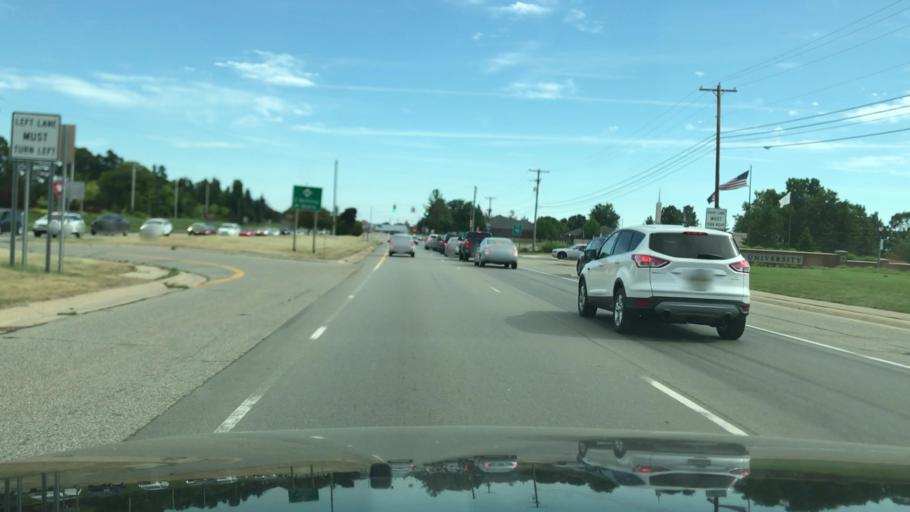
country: US
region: Michigan
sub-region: Kent County
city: East Grand Rapids
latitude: 42.9796
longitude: -85.5908
